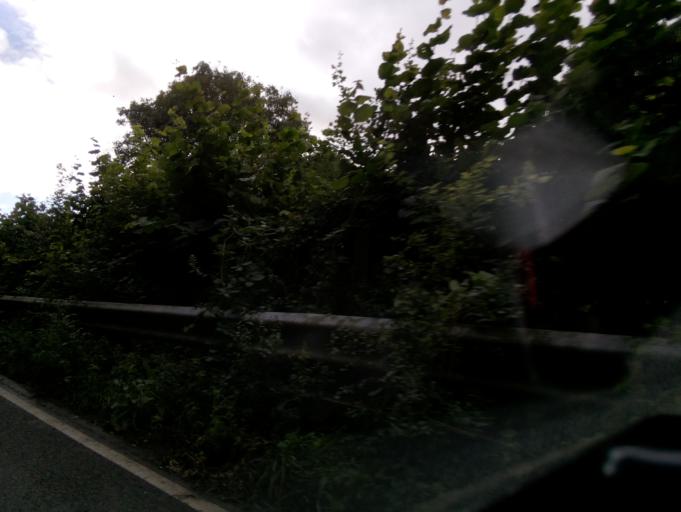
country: GB
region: England
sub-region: Devon
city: Modbury
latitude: 50.3262
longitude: -3.8423
